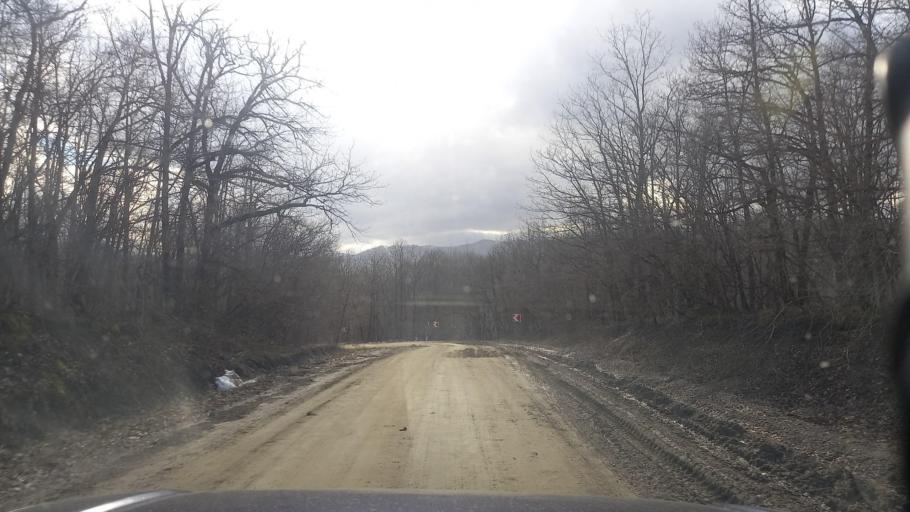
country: RU
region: Krasnodarskiy
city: Smolenskaya
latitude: 44.5759
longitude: 38.8065
